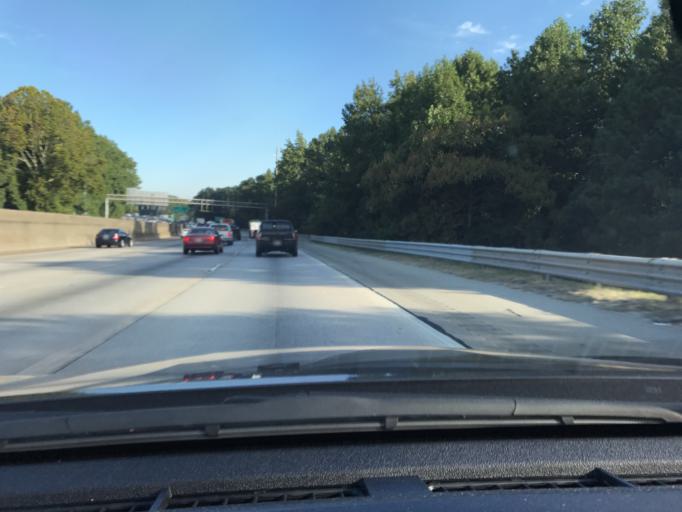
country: US
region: Georgia
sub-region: DeKalb County
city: Avondale Estates
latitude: 33.7699
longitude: -84.2327
